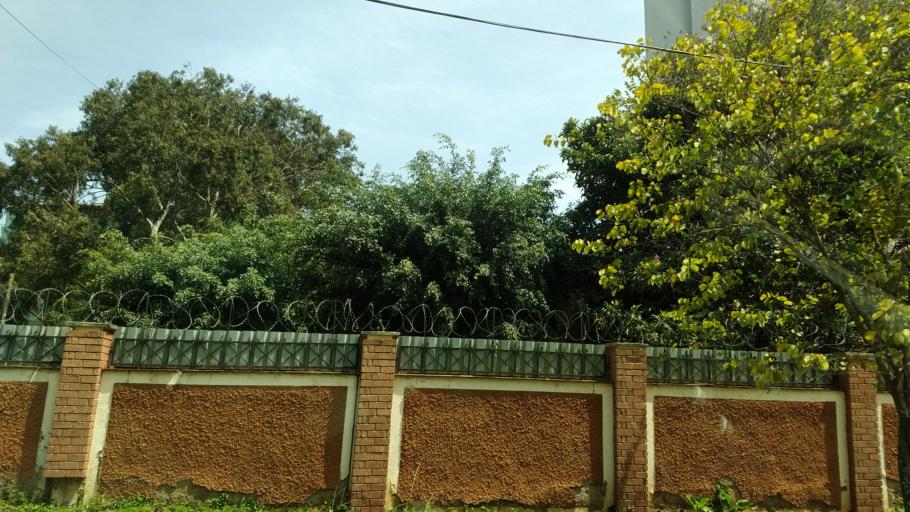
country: KE
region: Nairobi Area
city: Nairobi
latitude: -1.2964
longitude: 36.7864
